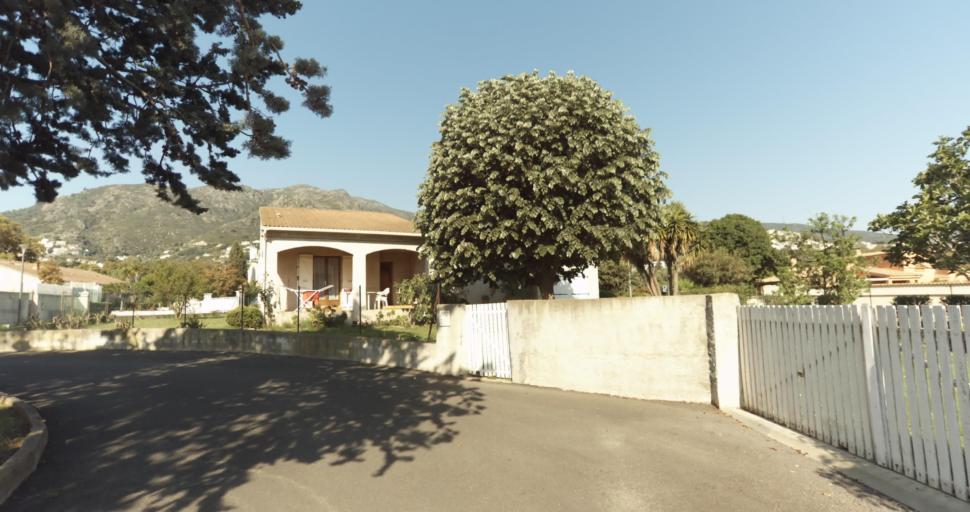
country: FR
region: Corsica
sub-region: Departement de la Haute-Corse
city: Biguglia
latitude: 42.6336
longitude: 9.4310
